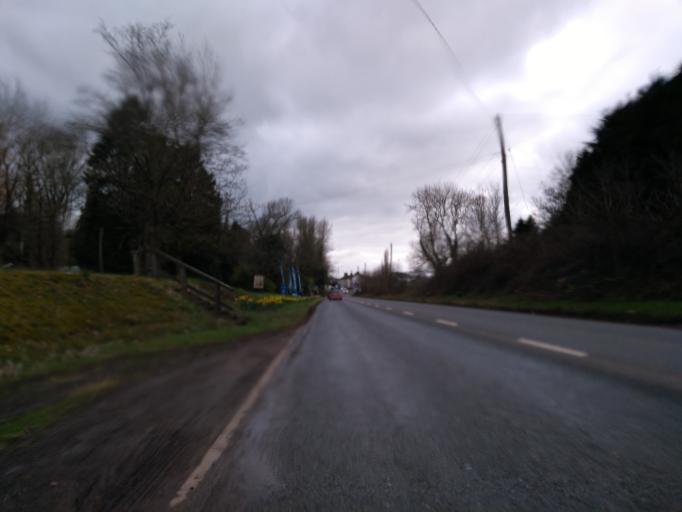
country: GB
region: England
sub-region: Devon
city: Exeter
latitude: 50.7625
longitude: -3.5643
